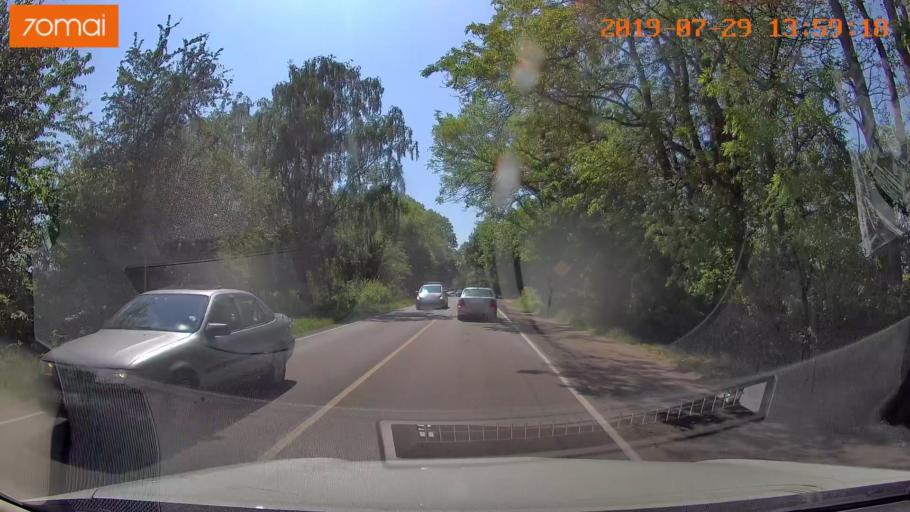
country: RU
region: Kaliningrad
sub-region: Gorod Kaliningrad
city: Baltiysk
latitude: 54.6857
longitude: 19.9329
